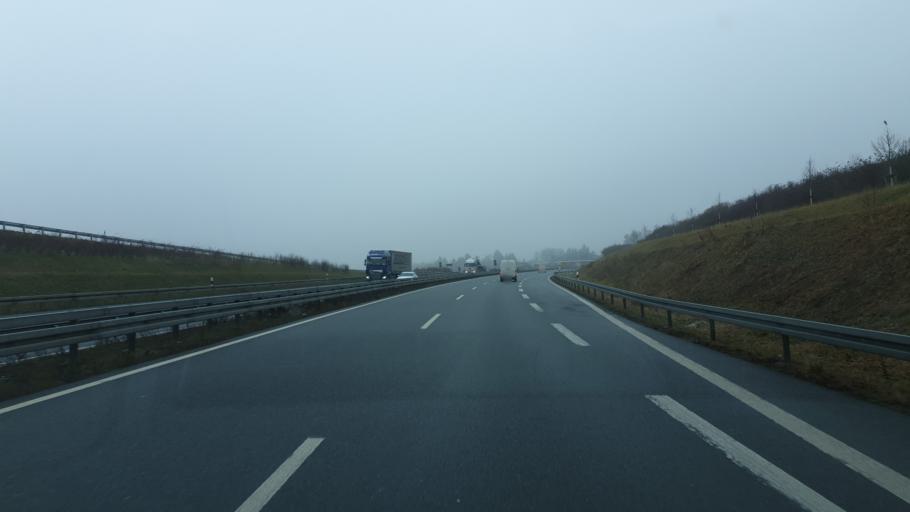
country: DE
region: Saxony
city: Hilbersdorf
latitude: 50.8007
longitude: 12.9738
